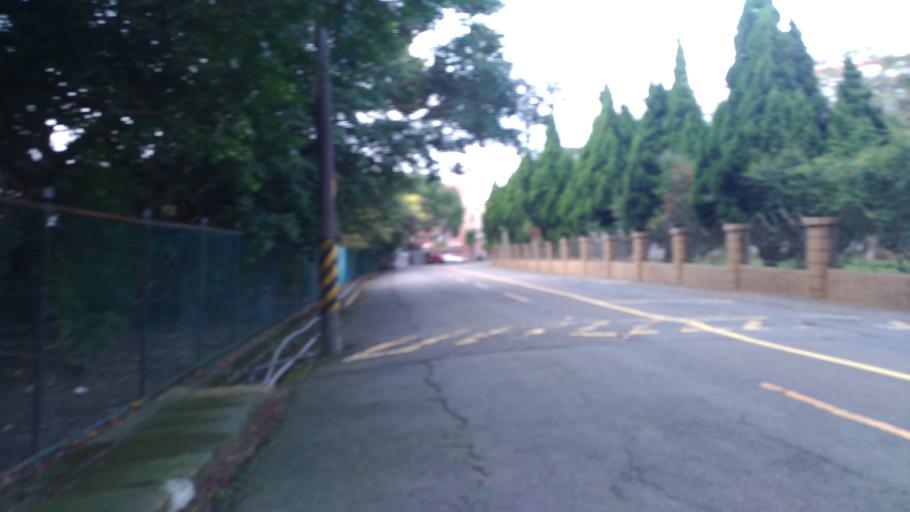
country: TW
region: Taiwan
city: Daxi
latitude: 24.8824
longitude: 121.1739
